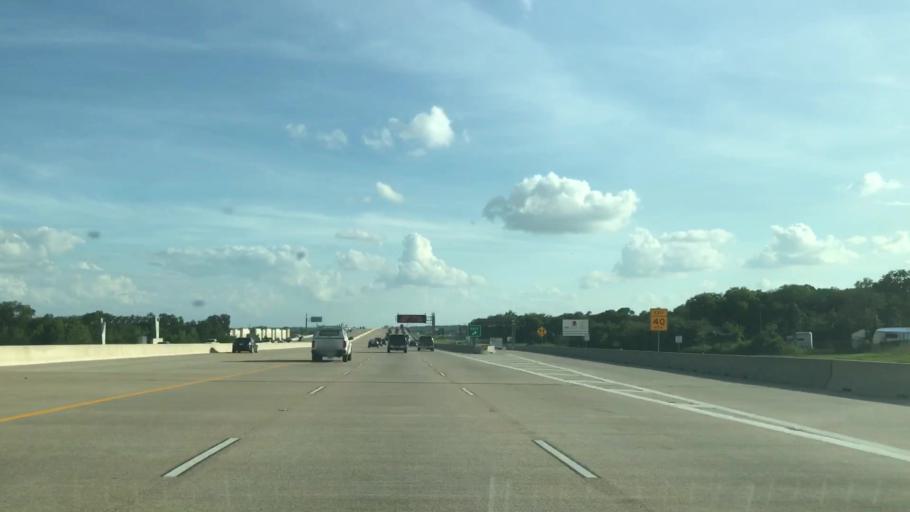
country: US
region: Texas
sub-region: Dallas County
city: Grand Prairie
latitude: 32.8086
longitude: -97.0185
